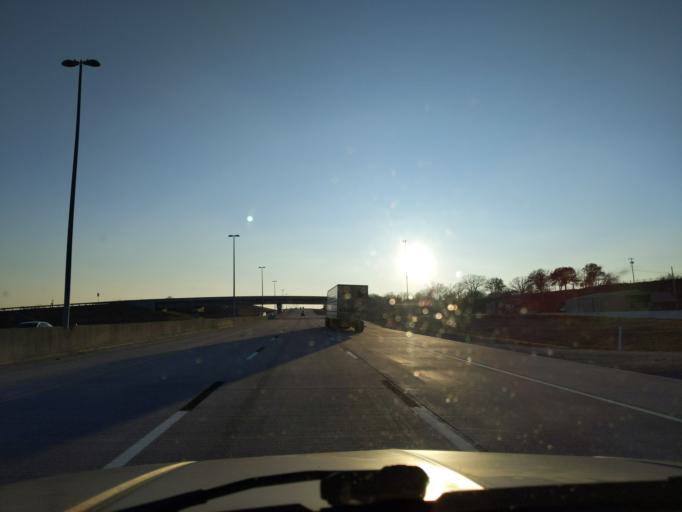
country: US
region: Oklahoma
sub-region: Creek County
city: Kellyville
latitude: 35.9459
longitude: -96.2514
